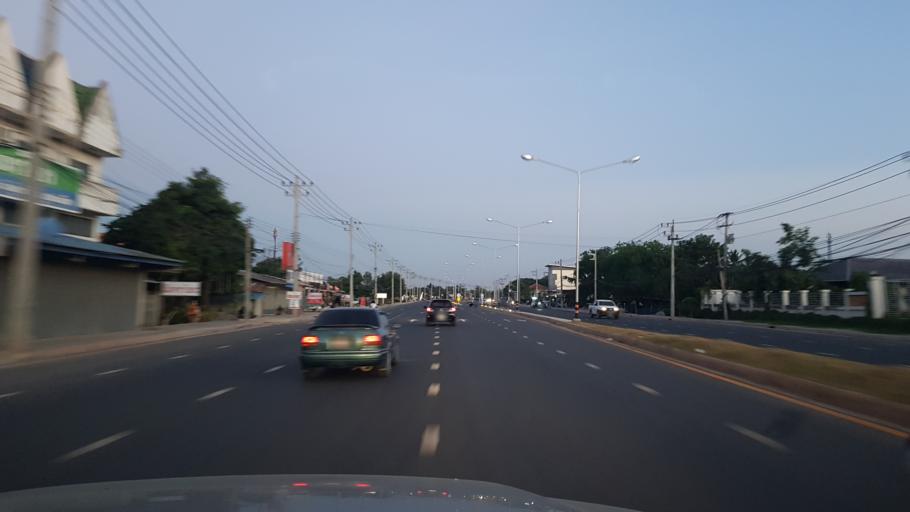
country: TH
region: Chaiyaphum
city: Phu Khiao
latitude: 16.3626
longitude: 102.1442
